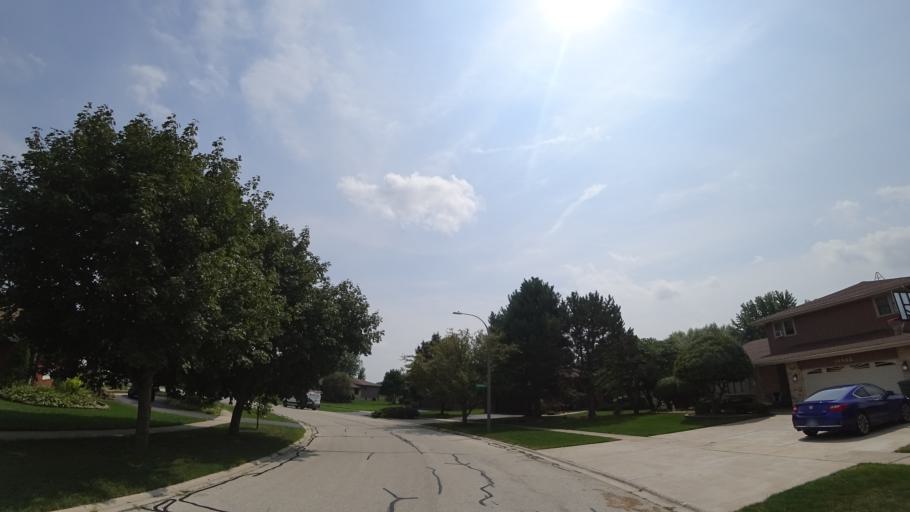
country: US
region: Illinois
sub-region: Will County
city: Goodings Grove
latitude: 41.6268
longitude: -87.9059
